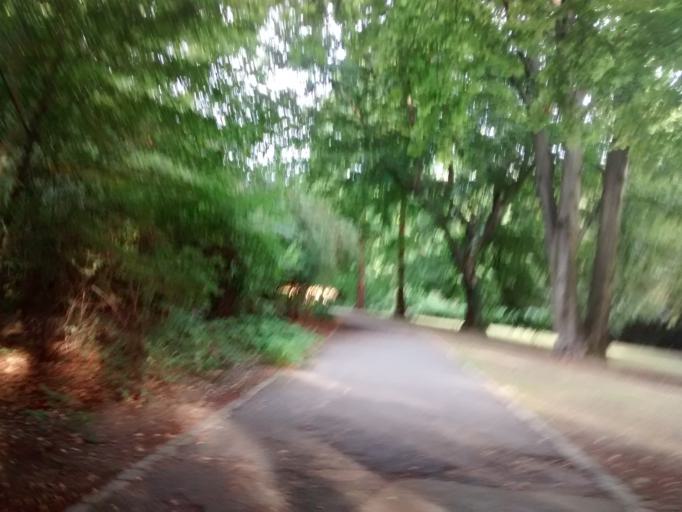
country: DE
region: Berlin
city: Reinickendorf
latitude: 52.5542
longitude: 13.3324
